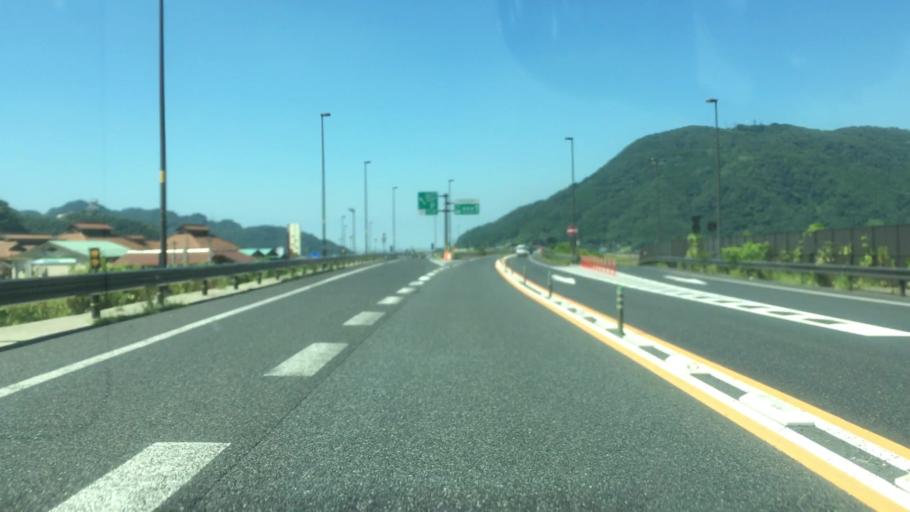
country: JP
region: Tottori
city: Tottori
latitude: 35.3917
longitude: 134.2033
